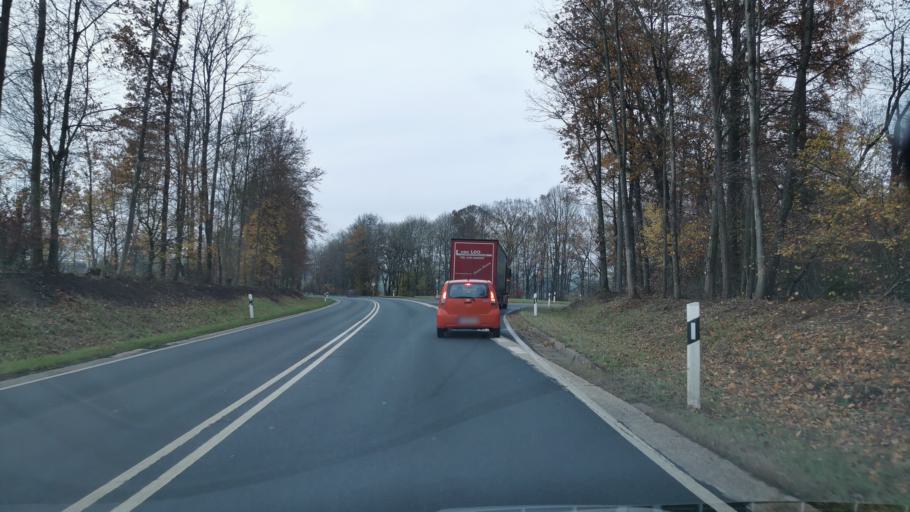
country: DE
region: Rheinland-Pfalz
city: Dohr
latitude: 50.1411
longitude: 7.1313
